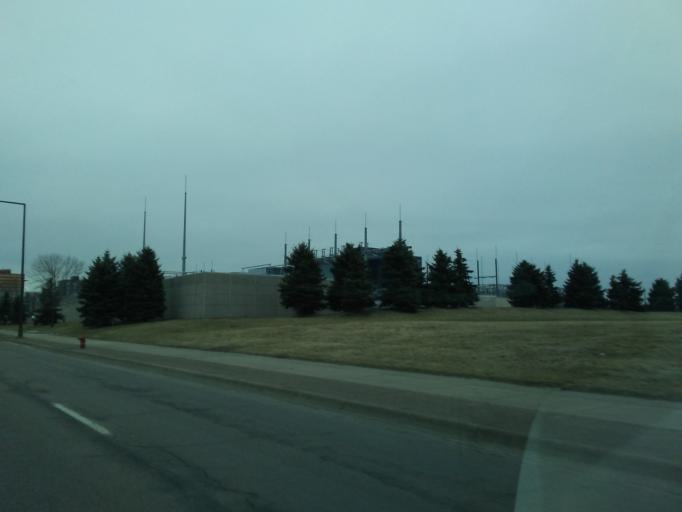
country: US
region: Minnesota
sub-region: Hennepin County
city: Richfield
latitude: 44.8587
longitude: -93.2316
